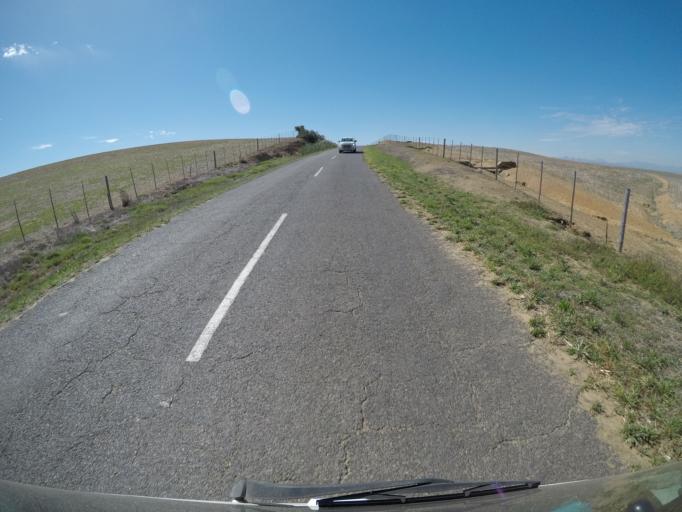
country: ZA
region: Western Cape
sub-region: City of Cape Town
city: Sunset Beach
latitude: -33.7426
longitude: 18.5615
